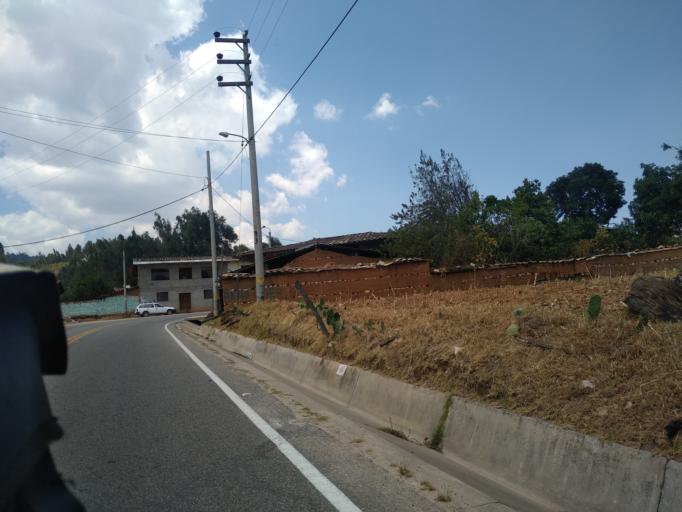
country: PE
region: Cajamarca
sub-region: San Marcos
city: San Marcos
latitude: -7.2828
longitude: -78.2176
